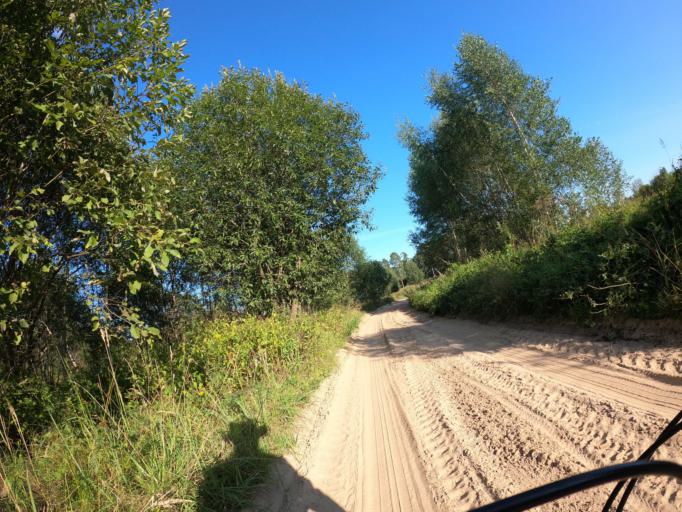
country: RU
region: Moskovskaya
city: Stupino
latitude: 54.8674
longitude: 38.1107
